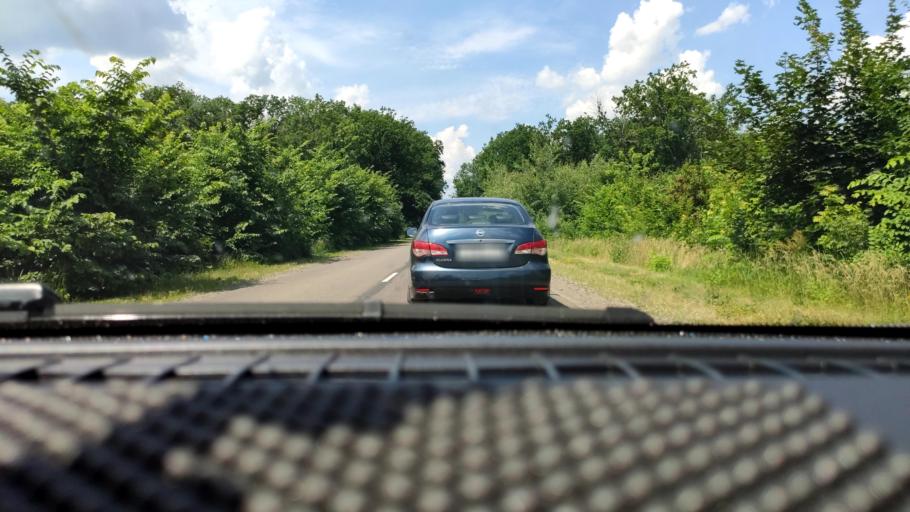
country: RU
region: Voronezj
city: Podkletnoye
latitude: 51.6373
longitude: 39.5037
